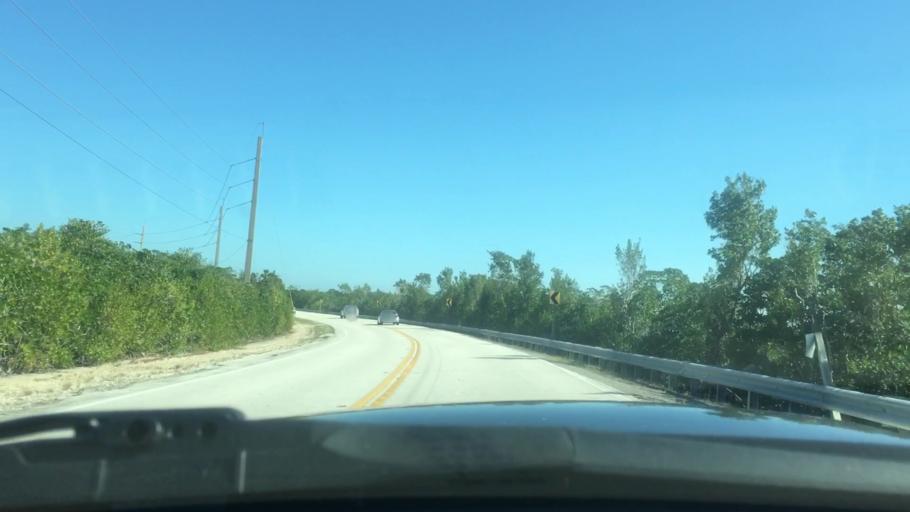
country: US
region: Florida
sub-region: Monroe County
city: North Key Largo
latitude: 25.2793
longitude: -80.3402
